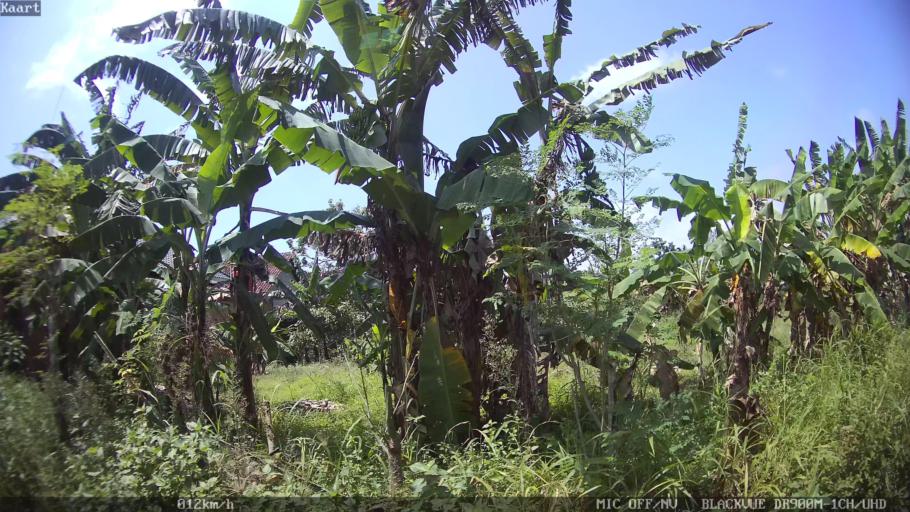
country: ID
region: Lampung
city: Kedaton
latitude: -5.3542
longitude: 105.2772
